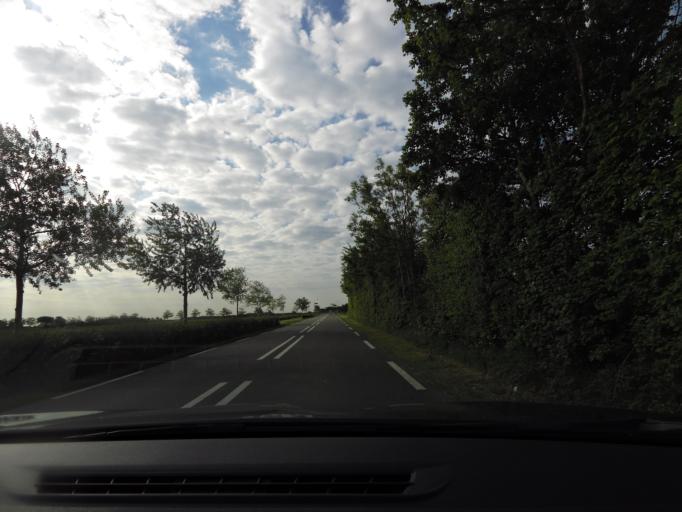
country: NL
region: Zeeland
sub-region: Schouwen-Duiveland
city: Renesse
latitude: 51.7201
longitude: 3.7960
